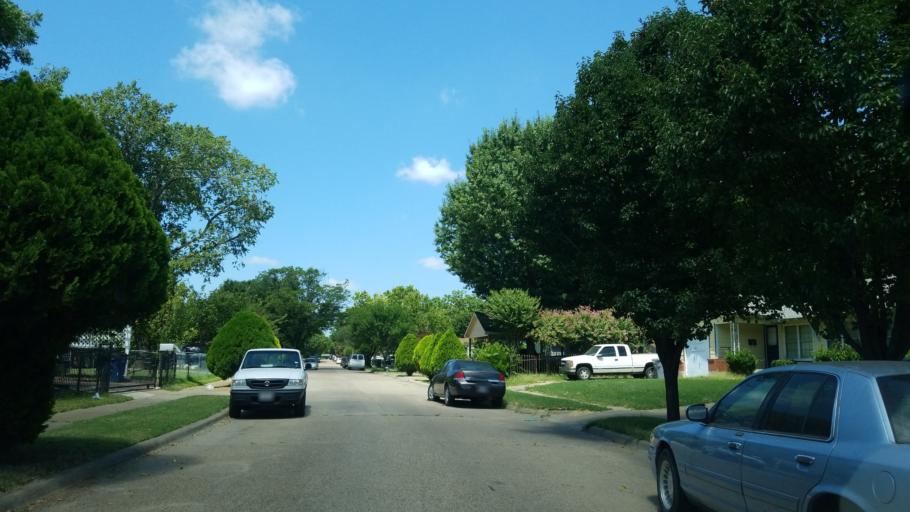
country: US
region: Texas
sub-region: Dallas County
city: Balch Springs
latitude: 32.7373
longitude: -96.6952
